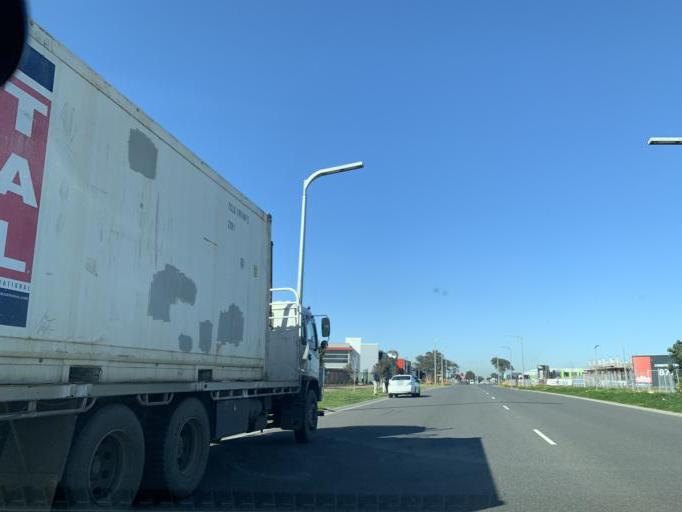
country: AU
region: Victoria
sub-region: Greater Dandenong
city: Dandenong
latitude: -38.0096
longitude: 145.1976
